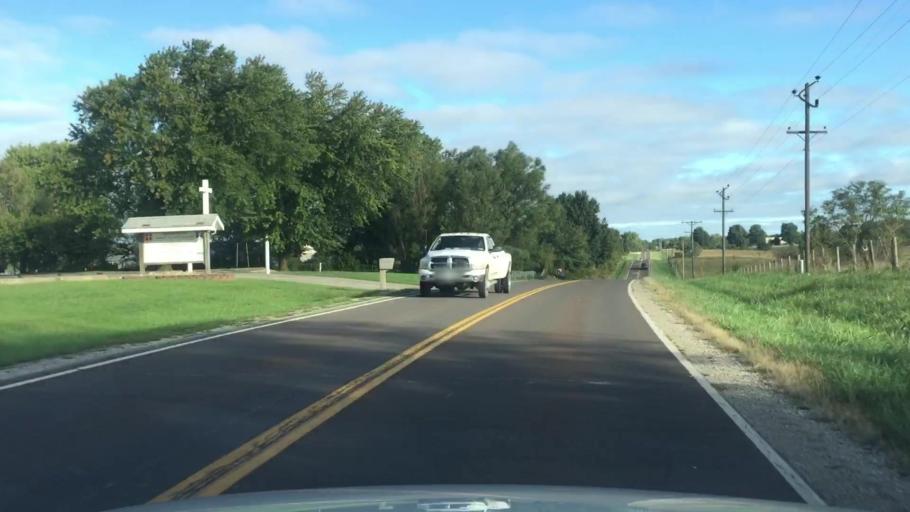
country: US
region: Missouri
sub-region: Howard County
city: New Franklin
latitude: 39.0392
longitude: -92.7444
